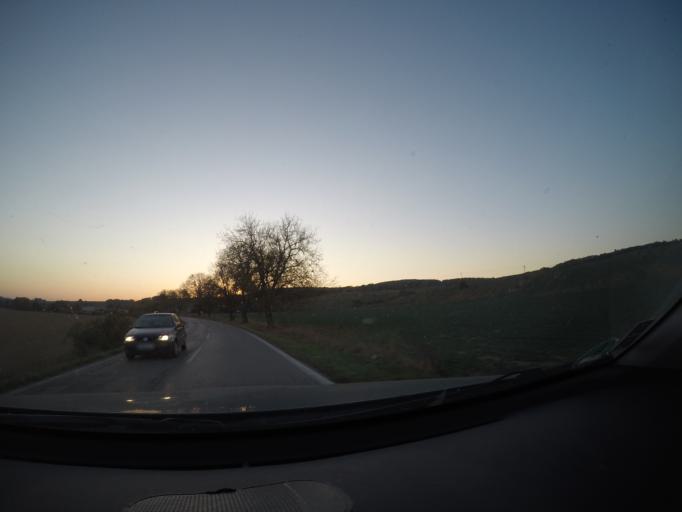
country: SK
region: Nitriansky
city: Nemsova
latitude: 48.9562
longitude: 18.0960
